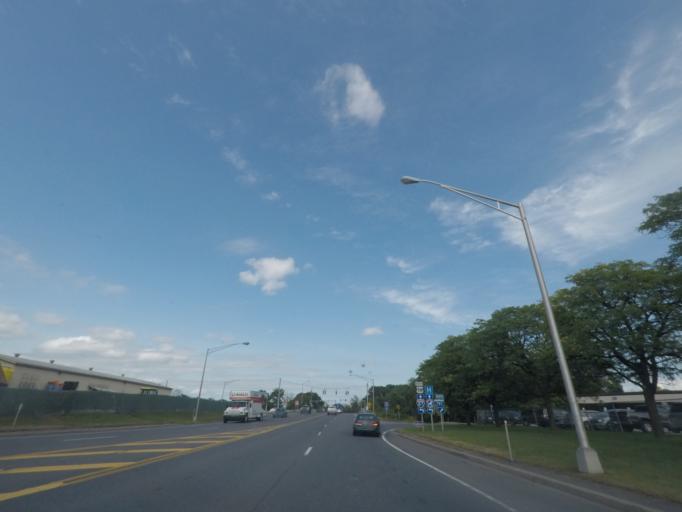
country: US
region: New York
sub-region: Albany County
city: Albany
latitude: 42.6315
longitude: -73.7758
